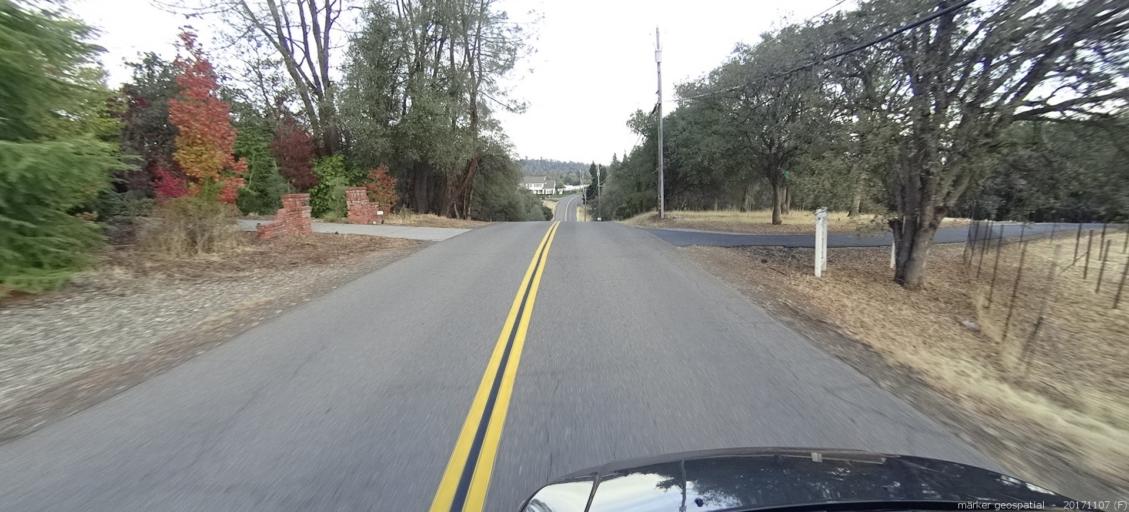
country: US
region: California
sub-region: Shasta County
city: Shasta
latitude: 40.5416
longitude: -122.4794
